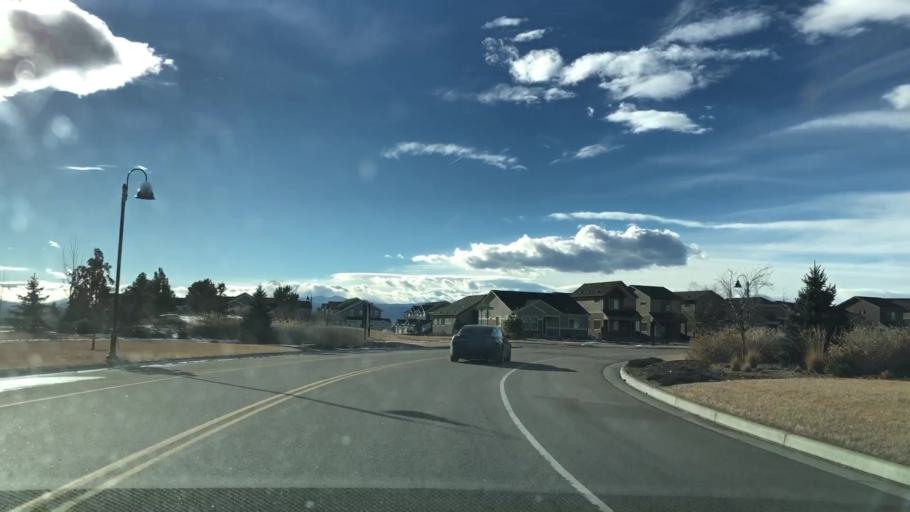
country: US
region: Colorado
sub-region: Larimer County
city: Loveland
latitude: 40.4182
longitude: -105.0175
